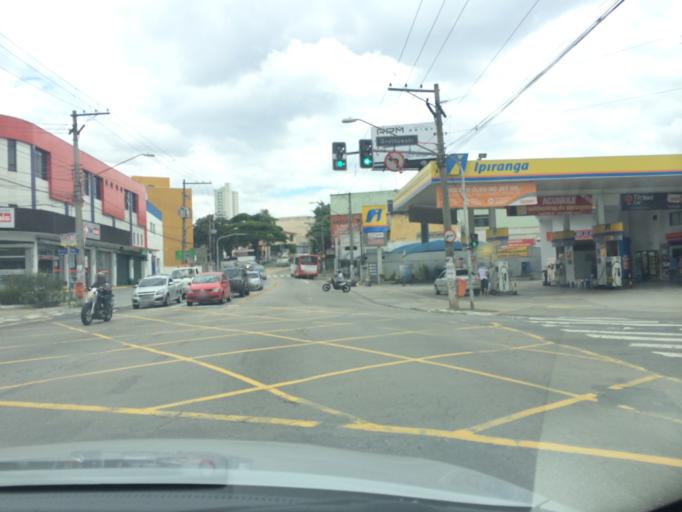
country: BR
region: Sao Paulo
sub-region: Guarulhos
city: Guarulhos
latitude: -23.4578
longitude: -46.5206
